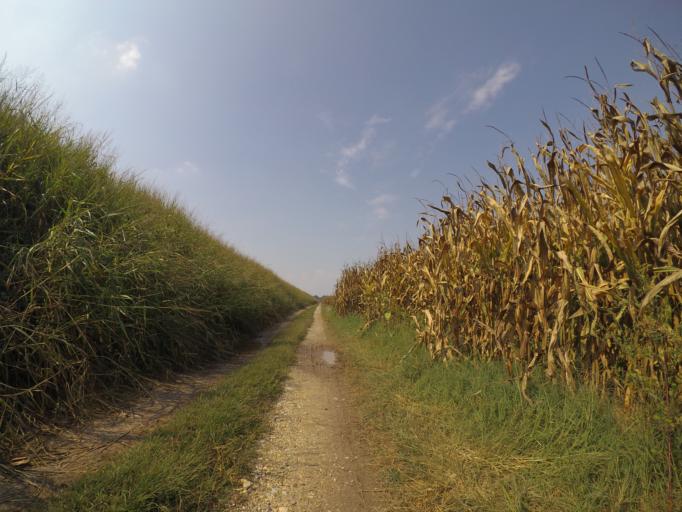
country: IT
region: Friuli Venezia Giulia
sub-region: Provincia di Udine
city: Varmo
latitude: 45.8858
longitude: 12.9674
